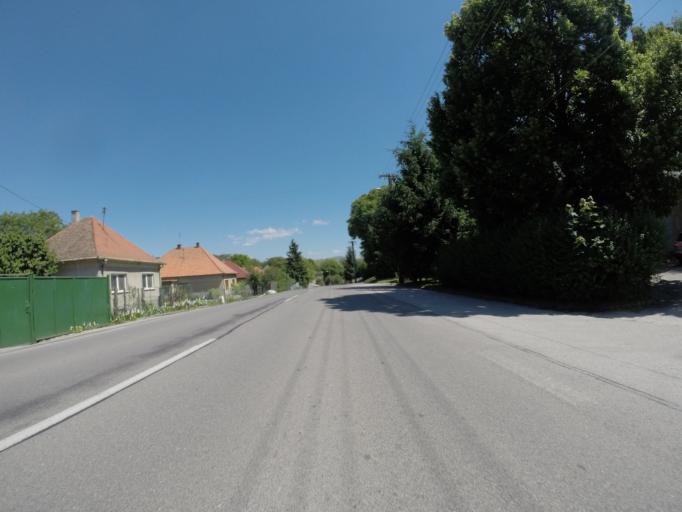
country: SK
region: Nitriansky
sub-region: Okres Nitra
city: Nitra
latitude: 48.5265
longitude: 18.0573
